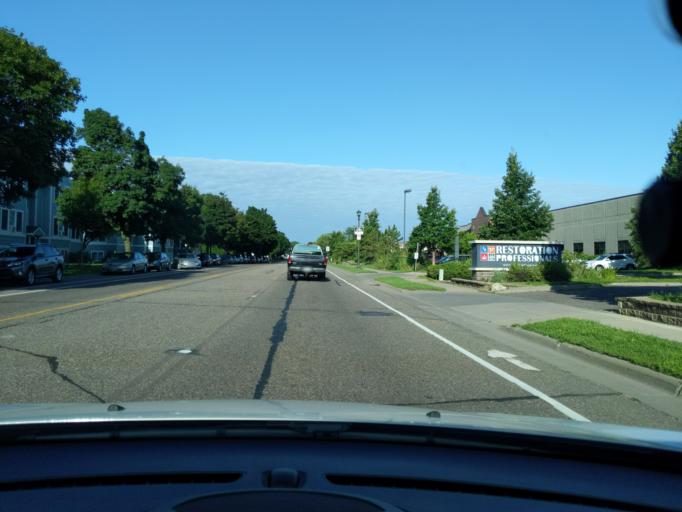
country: US
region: Minnesota
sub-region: Ramsey County
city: Saint Paul
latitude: 44.9630
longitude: -93.1214
